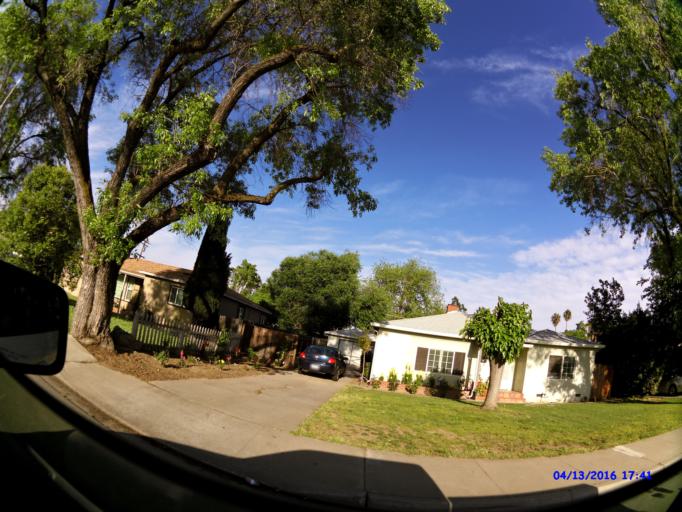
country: US
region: California
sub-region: Stanislaus County
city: Bystrom
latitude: 37.6464
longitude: -120.9573
